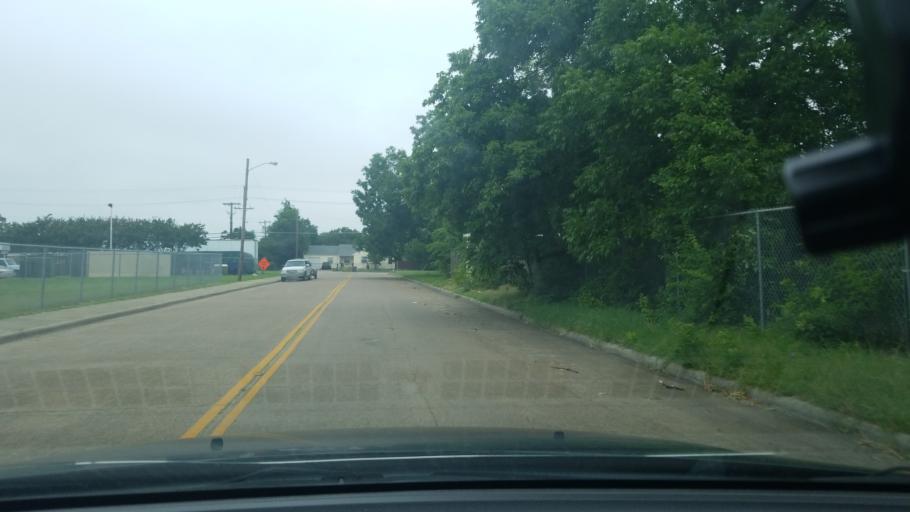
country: US
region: Texas
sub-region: Dallas County
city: Balch Springs
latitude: 32.7569
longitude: -96.6851
